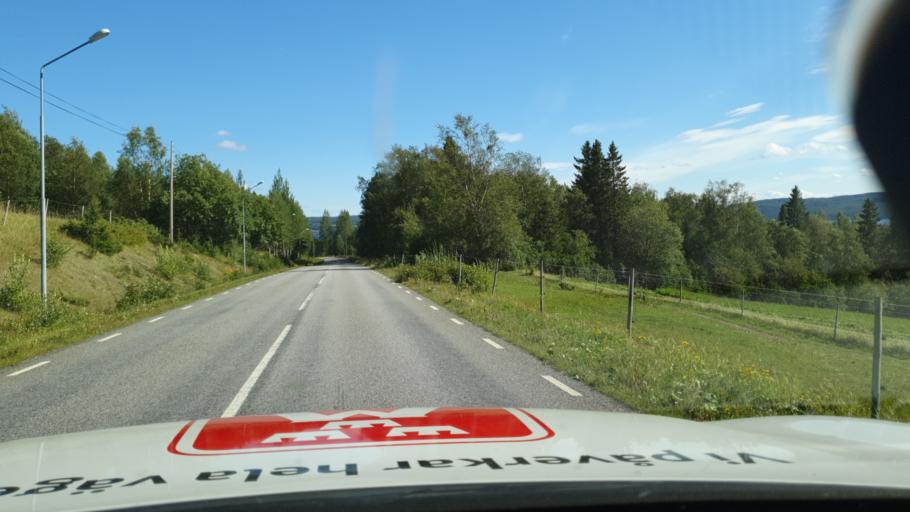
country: SE
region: Jaemtland
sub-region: Are Kommun
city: Are
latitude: 63.4680
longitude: 13.2912
